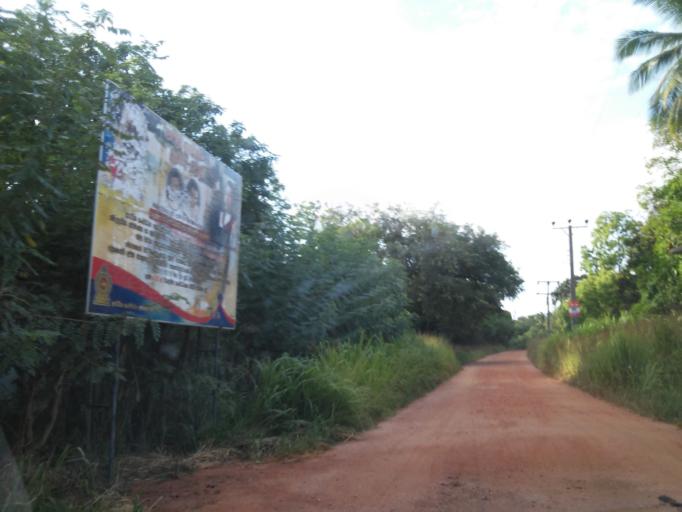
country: LK
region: Central
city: Sigiriya
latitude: 8.1763
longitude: 80.6675
